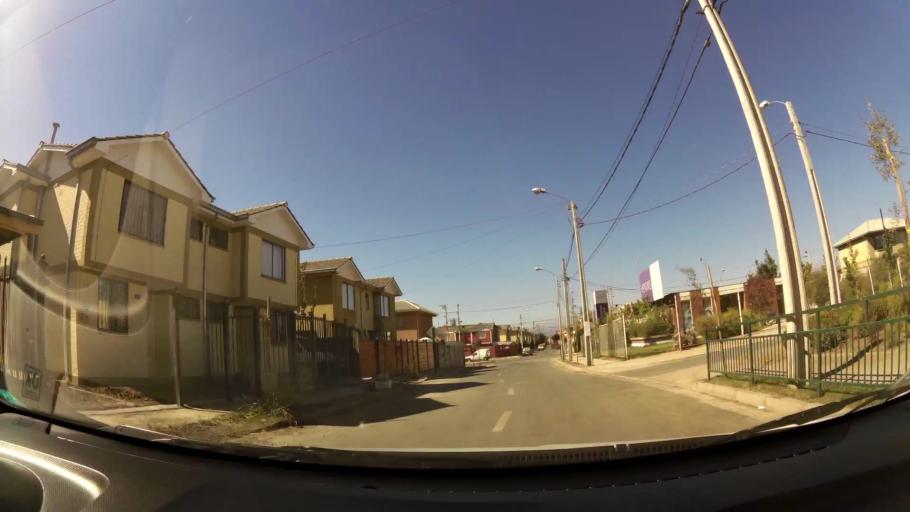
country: CL
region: O'Higgins
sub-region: Provincia de Cachapoal
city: Rancagua
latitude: -34.1767
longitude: -70.7700
